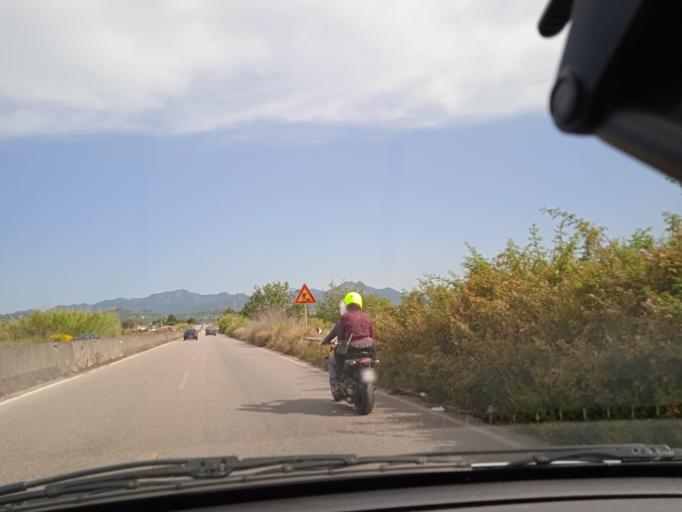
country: IT
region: Sicily
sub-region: Messina
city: Milazzo
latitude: 38.1919
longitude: 15.2594
